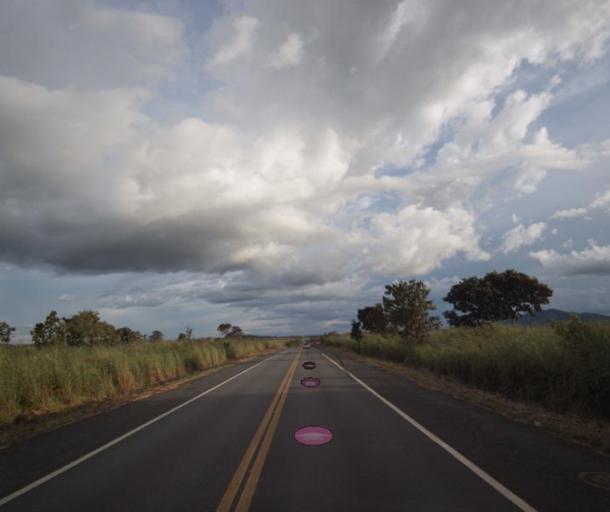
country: BR
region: Goias
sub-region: Barro Alto
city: Barro Alto
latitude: -14.8406
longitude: -48.6383
